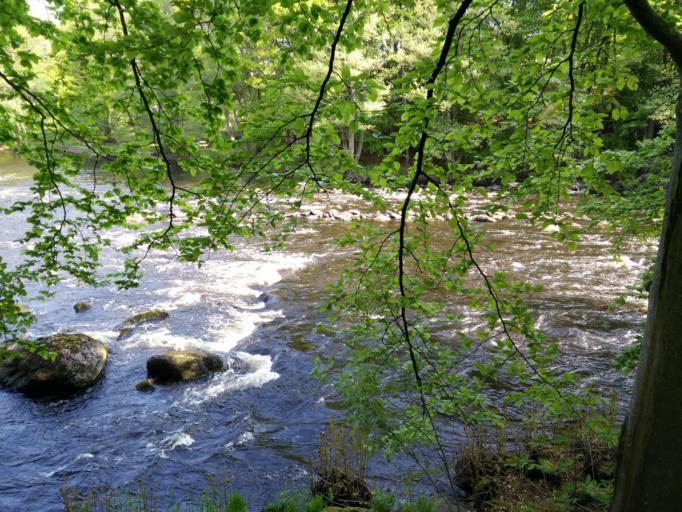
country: SE
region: Blekinge
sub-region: Karlshamns Kommun
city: Morrum
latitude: 56.2025
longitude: 14.7493
